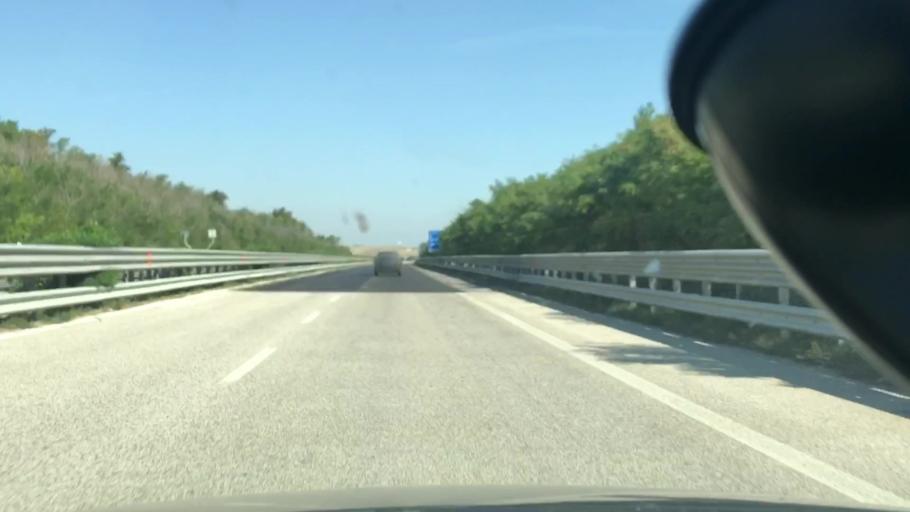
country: IT
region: Apulia
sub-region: Provincia di Foggia
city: Ordona
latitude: 41.2935
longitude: 15.5541
